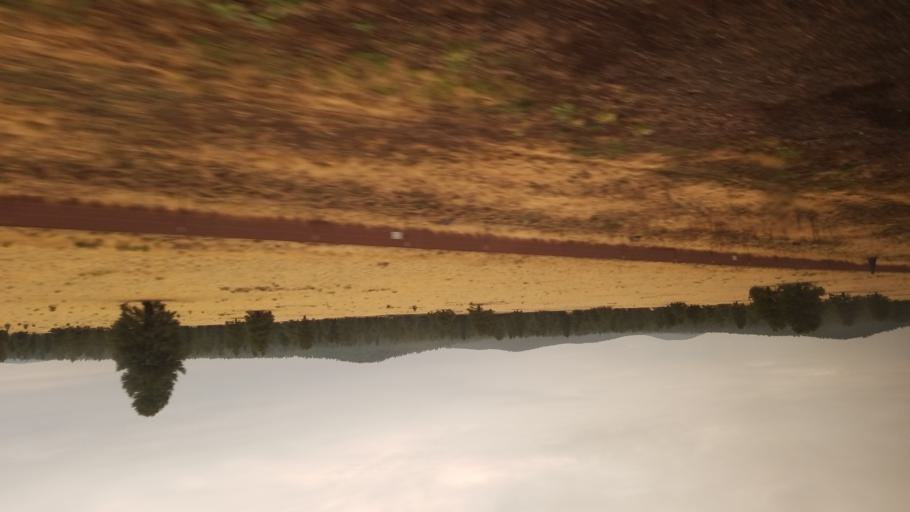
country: US
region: Arizona
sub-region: Coconino County
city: Parks
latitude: 35.2260
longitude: -111.8061
